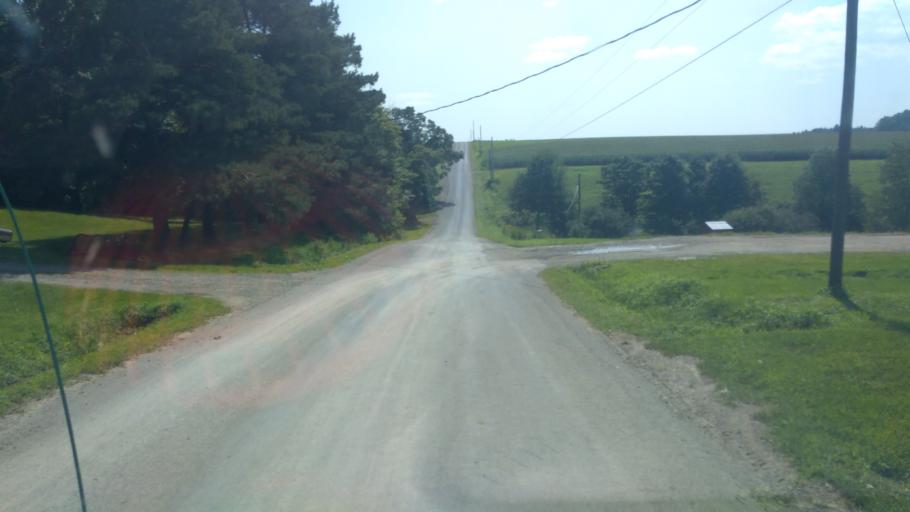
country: US
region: New York
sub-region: Steuben County
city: Canisteo
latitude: 42.3421
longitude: -77.5775
